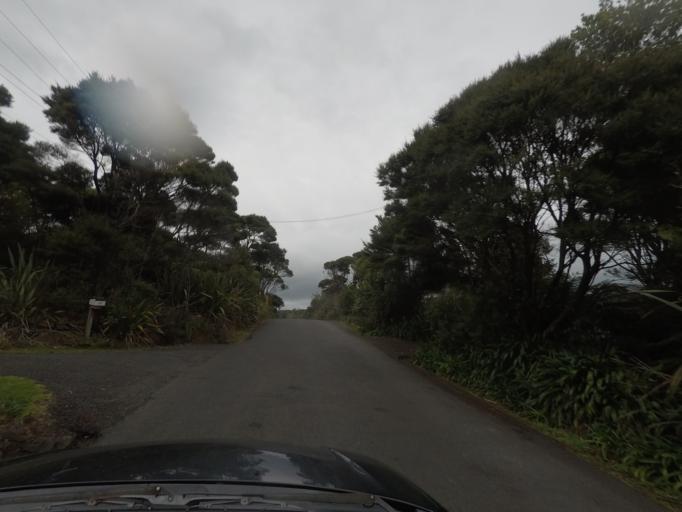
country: NZ
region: Auckland
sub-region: Auckland
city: Muriwai Beach
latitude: -36.9692
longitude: 174.4755
